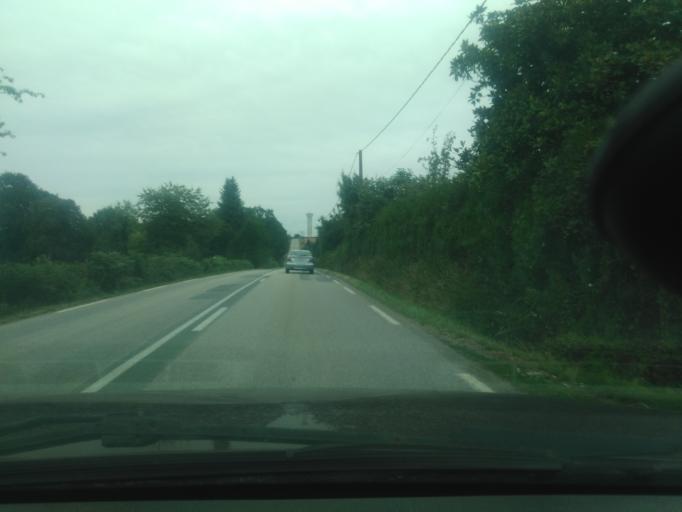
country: FR
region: Poitou-Charentes
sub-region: Departement des Deux-Sevres
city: Secondigny
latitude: 46.6211
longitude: -0.4663
